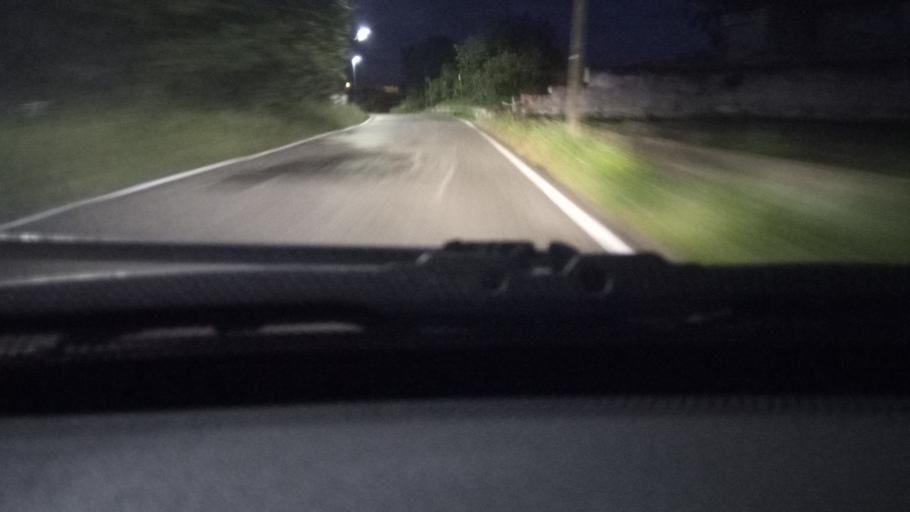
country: IT
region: Latium
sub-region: Provincia di Latina
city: Penitro
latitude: 41.2587
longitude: 13.6834
